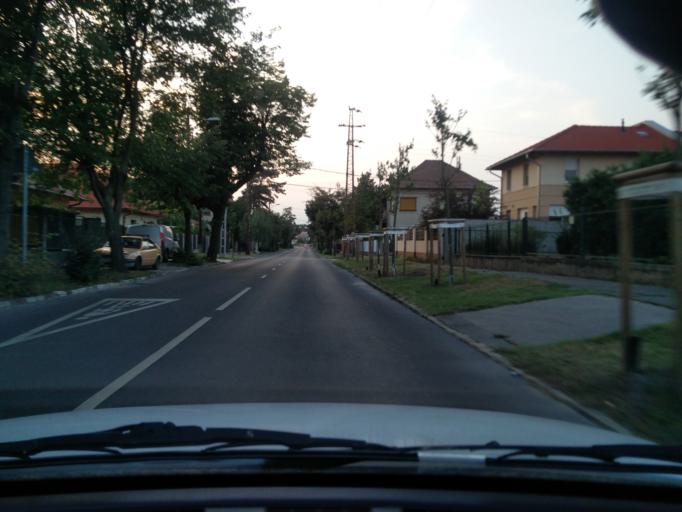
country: HU
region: Budapest
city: Budapest XXIII. keruelet
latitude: 47.3927
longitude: 19.1046
